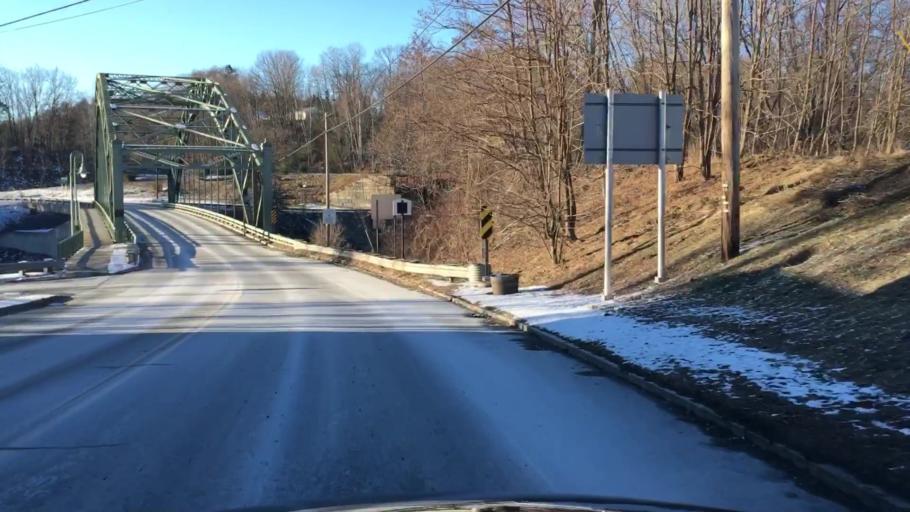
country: US
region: New Hampshire
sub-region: Grafton County
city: Woodsville
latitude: 44.1537
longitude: -72.0397
